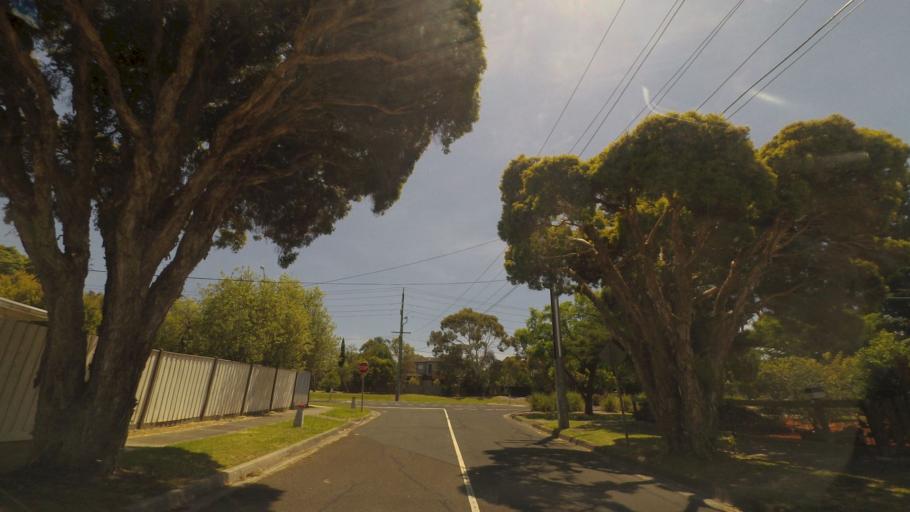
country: AU
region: Victoria
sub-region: Maroondah
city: Bayswater North
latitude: -37.8118
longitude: 145.2898
